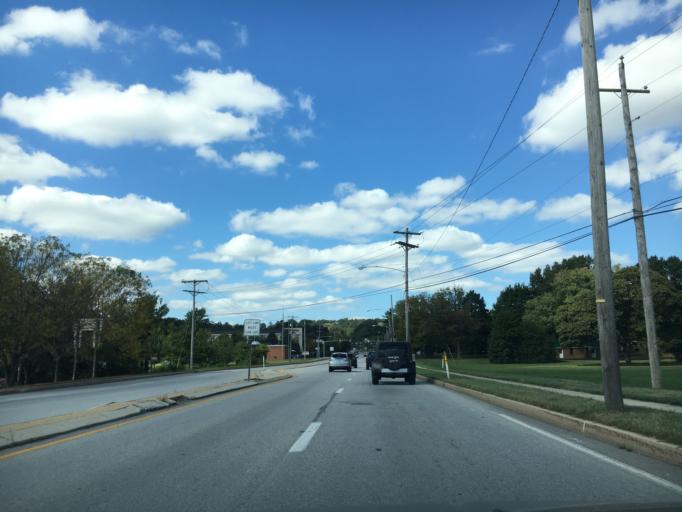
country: US
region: Pennsylvania
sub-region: York County
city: East York
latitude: 39.9889
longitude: -76.6692
